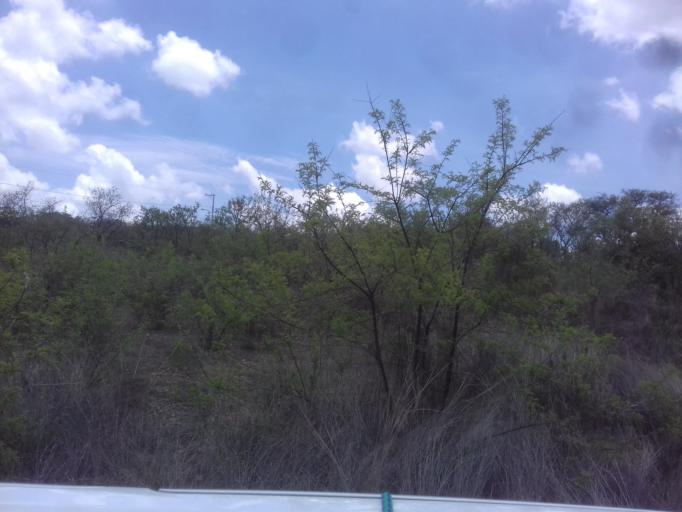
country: MX
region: Aguascalientes
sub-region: Aguascalientes
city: San Sebastian [Fraccionamiento]
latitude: 21.7866
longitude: -102.2515
